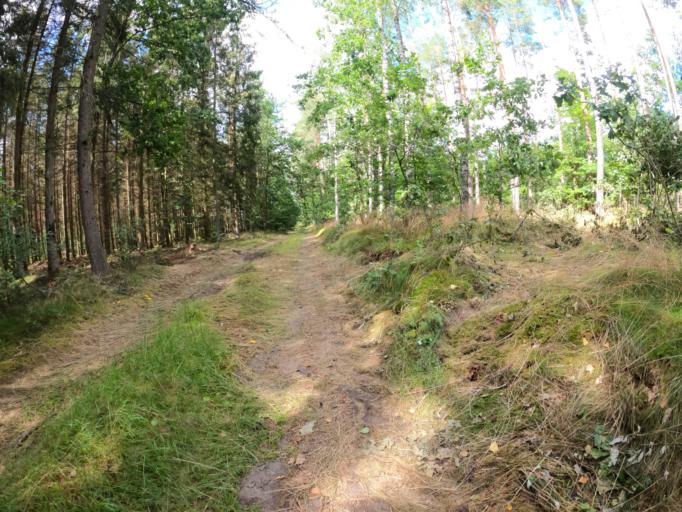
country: PL
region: West Pomeranian Voivodeship
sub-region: Powiat bialogardzki
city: Tychowo
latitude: 54.0132
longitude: 16.3551
